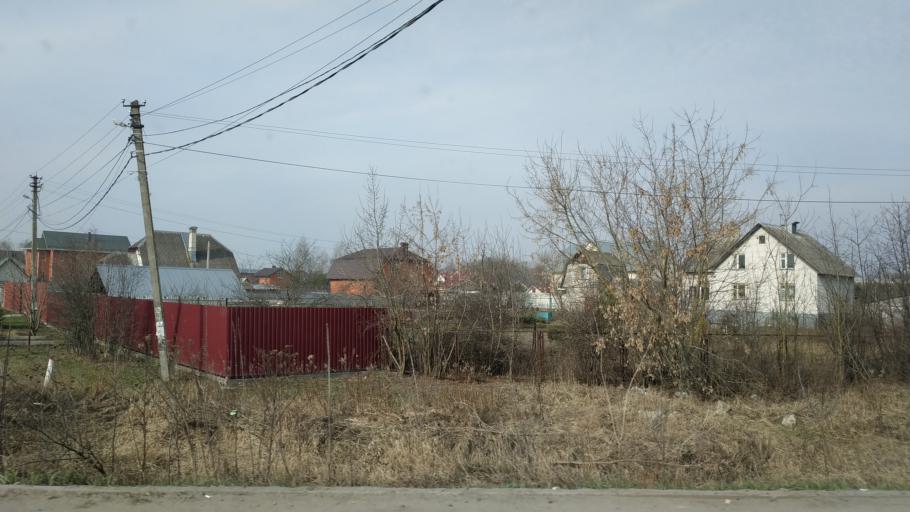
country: RU
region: Moskovskaya
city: Malyshevo
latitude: 55.4960
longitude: 38.3629
